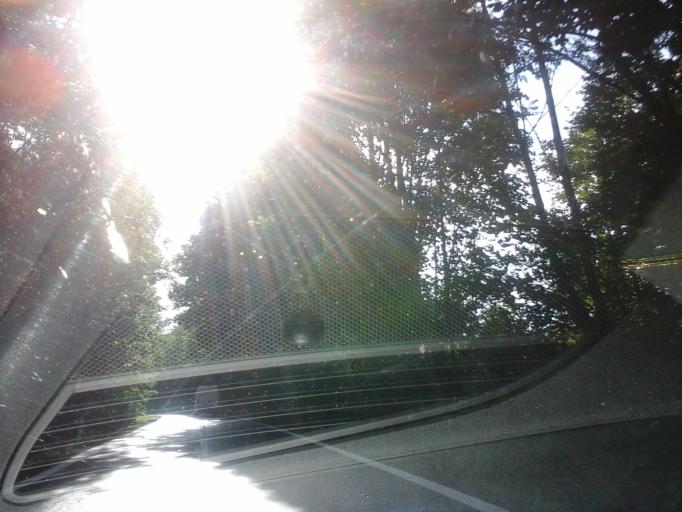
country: CZ
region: Olomoucky
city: Stity
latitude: 49.9627
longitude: 16.7310
